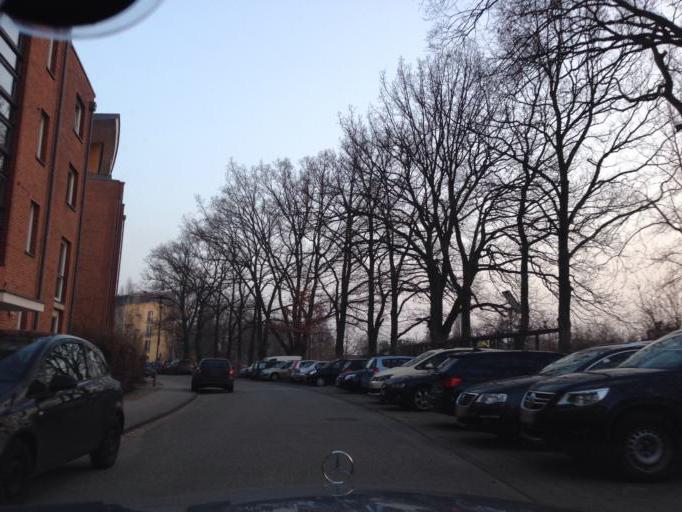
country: DE
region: Hamburg
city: Farmsen-Berne
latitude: 53.5950
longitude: 10.0996
